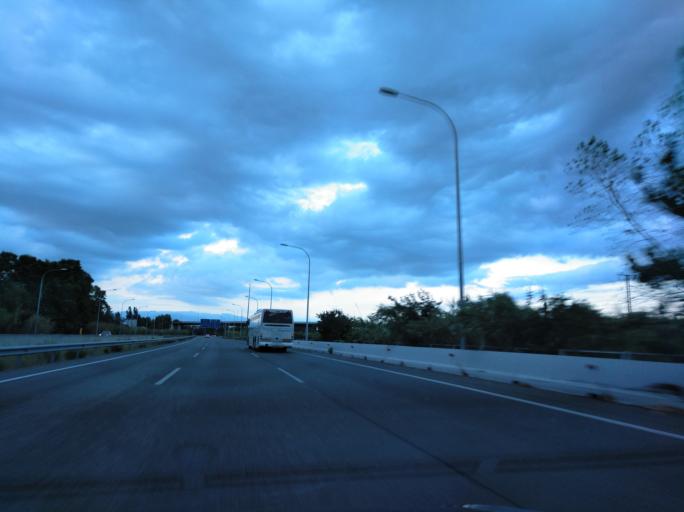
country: ES
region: Catalonia
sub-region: Provincia de Barcelona
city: Mollet del Valles
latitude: 41.5369
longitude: 2.2247
